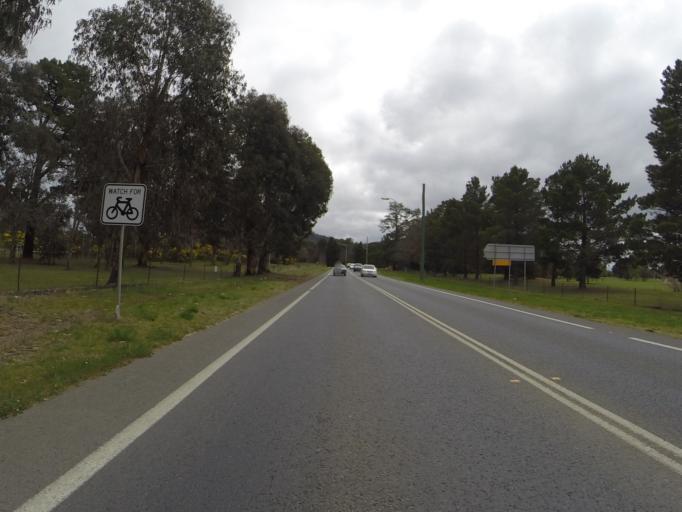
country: AU
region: Australian Capital Territory
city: Canberra
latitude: -35.2917
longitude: 149.1701
